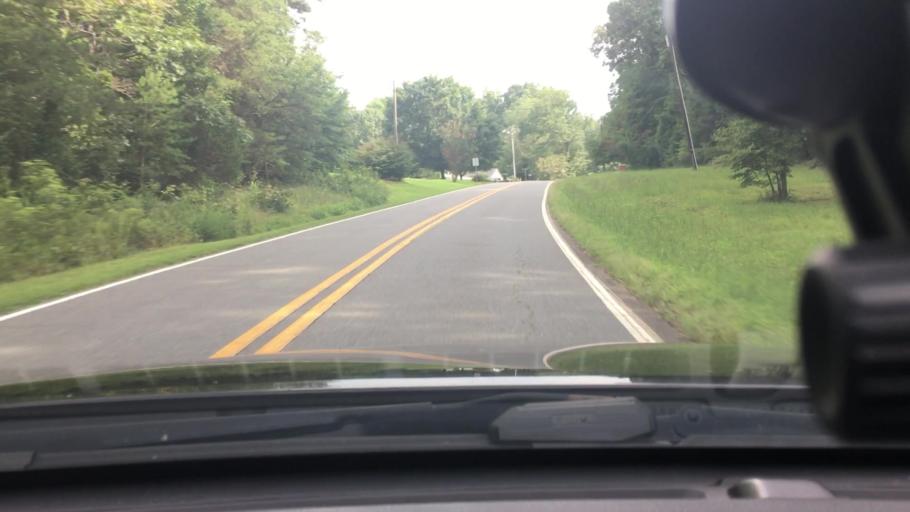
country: US
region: North Carolina
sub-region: Rutherford County
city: Rutherfordton
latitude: 35.3919
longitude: -81.9704
